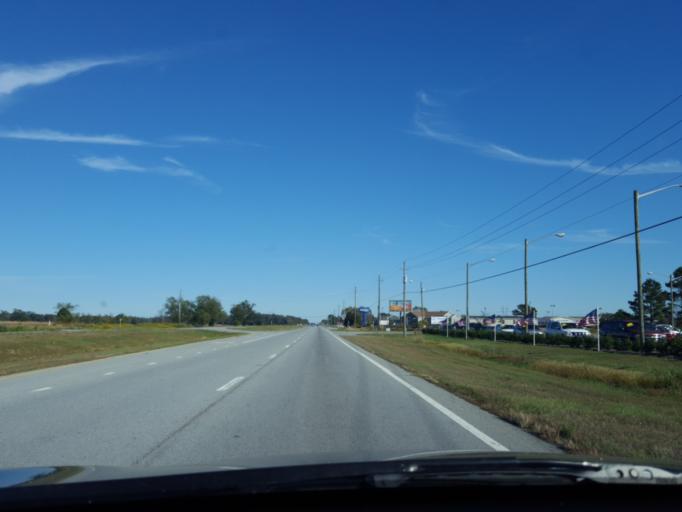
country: US
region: North Carolina
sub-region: Pitt County
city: Greenville
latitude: 35.6256
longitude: -77.3204
